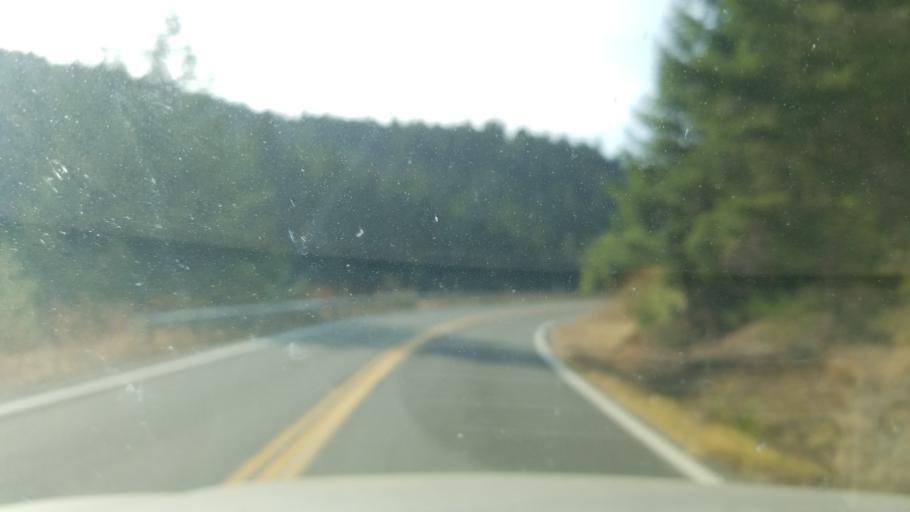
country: US
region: California
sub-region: Humboldt County
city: Redway
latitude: 40.2666
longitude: -123.8471
